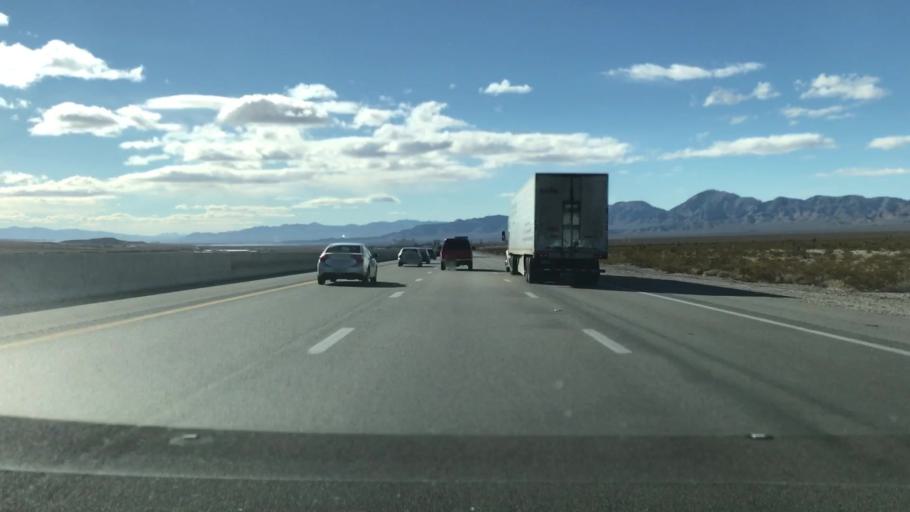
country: US
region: Nevada
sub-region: Clark County
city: Enterprise
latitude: 35.8095
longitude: -115.3070
